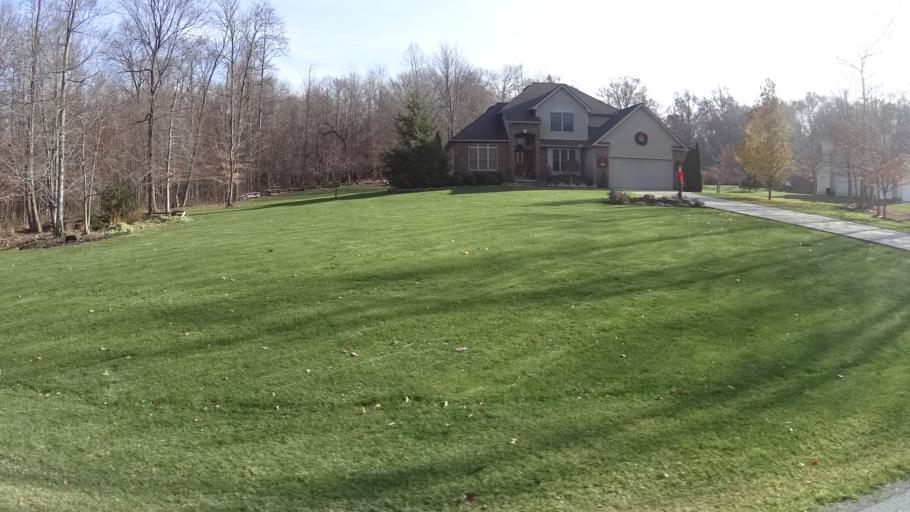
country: US
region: Ohio
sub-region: Lorain County
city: Grafton
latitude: 41.2176
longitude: -82.0349
